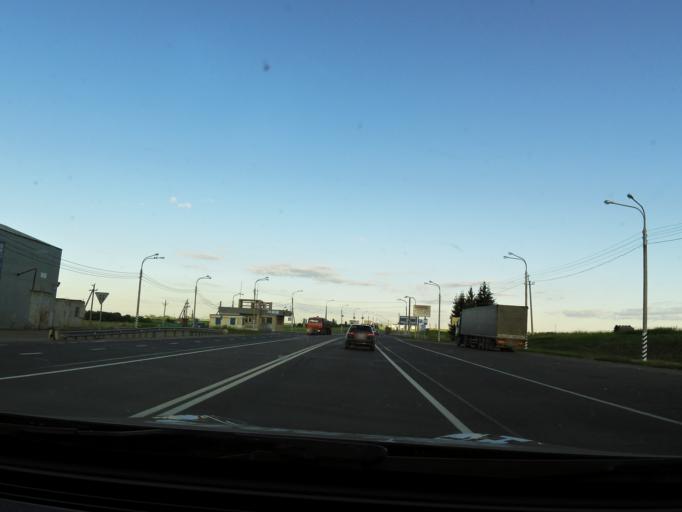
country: RU
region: Vologda
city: Vologda
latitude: 59.1715
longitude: 39.9075
